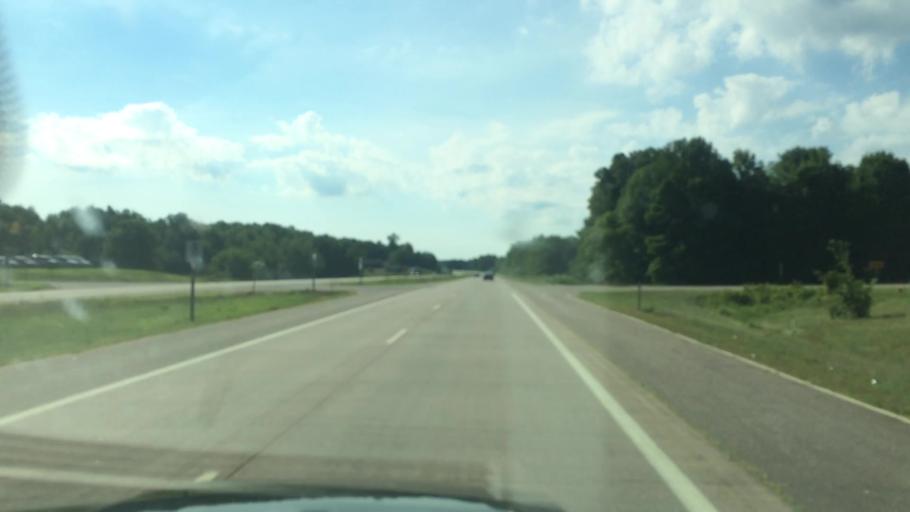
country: US
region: Wisconsin
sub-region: Shawano County
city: Wittenberg
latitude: 44.8108
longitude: -89.0420
